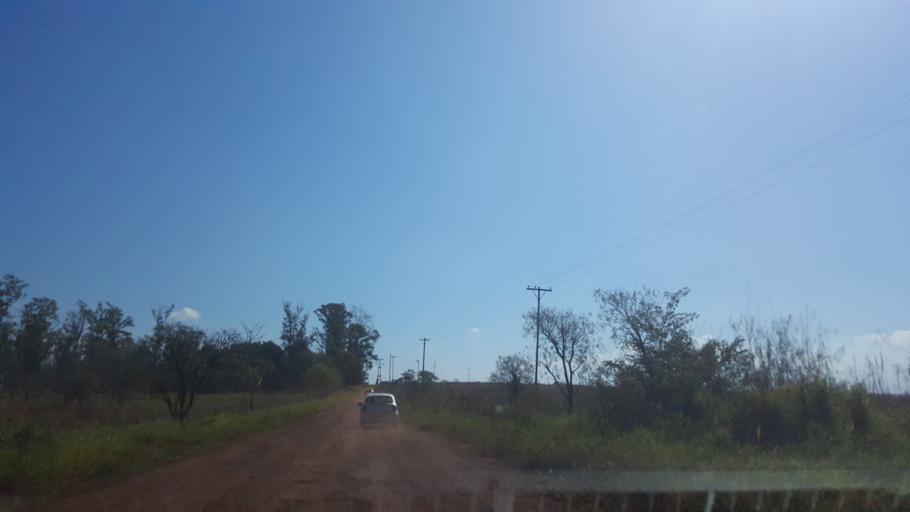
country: AR
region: Misiones
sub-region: Departamento de Capital
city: Posadas
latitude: -27.4206
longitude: -55.9994
